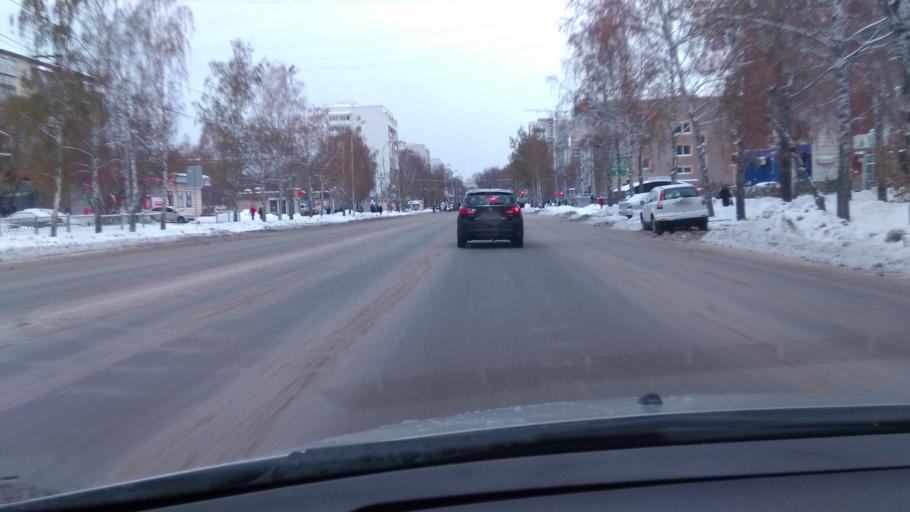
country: RU
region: Sverdlovsk
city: Sovkhoznyy
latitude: 56.8179
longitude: 60.5611
